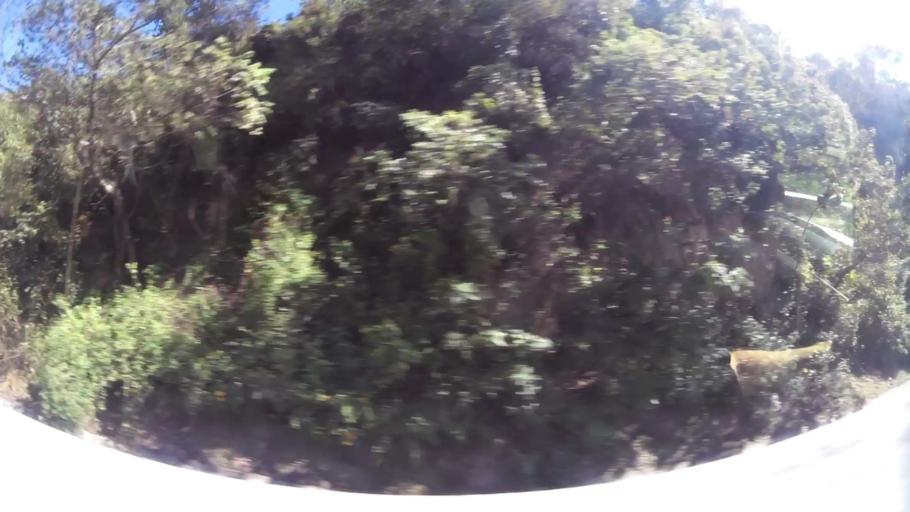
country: GT
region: Sacatepequez
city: Santa Lucia Milpas Altas
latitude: 14.5722
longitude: -90.6893
